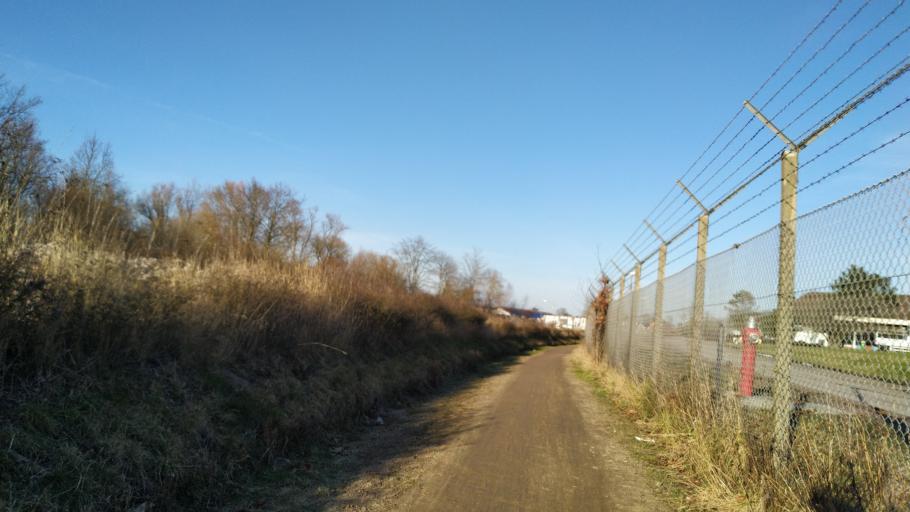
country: DE
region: Schleswig-Holstein
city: Neustadt in Holstein
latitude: 54.0997
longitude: 10.8004
